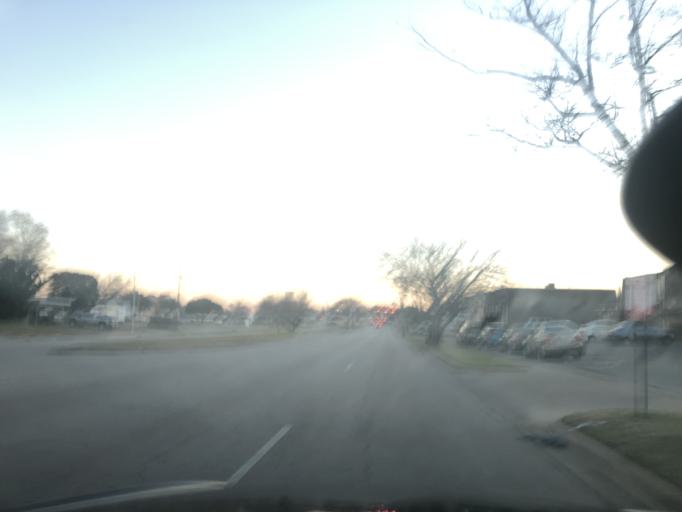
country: US
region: Texas
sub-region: Tarrant County
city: White Settlement
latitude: 32.7266
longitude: -97.4656
